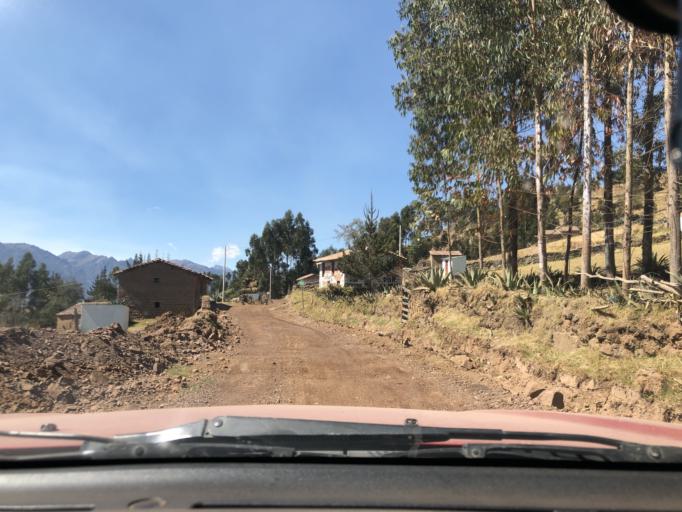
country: PE
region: Ayacucho
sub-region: Provincia de La Mar
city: Chilcas
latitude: -13.1695
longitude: -73.8522
